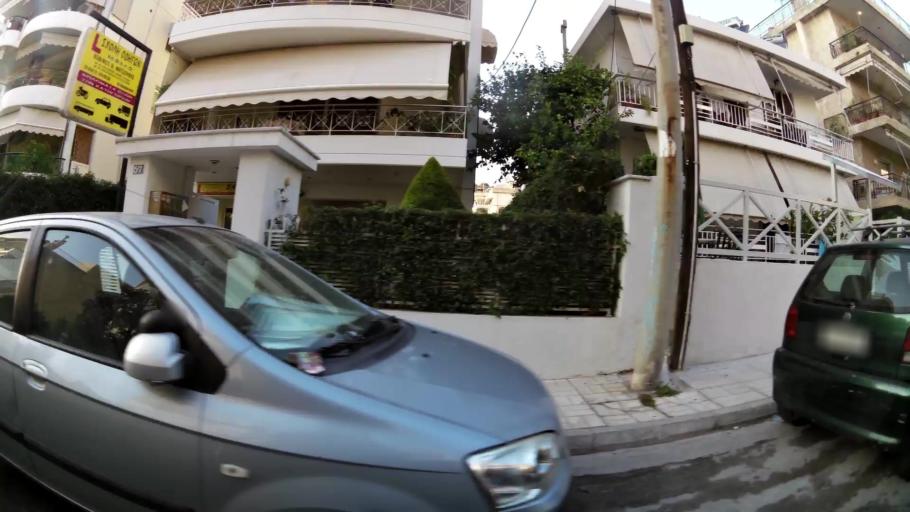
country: GR
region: Attica
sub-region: Nomarchia Athinas
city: Argyroupoli
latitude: 37.8983
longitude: 23.7648
